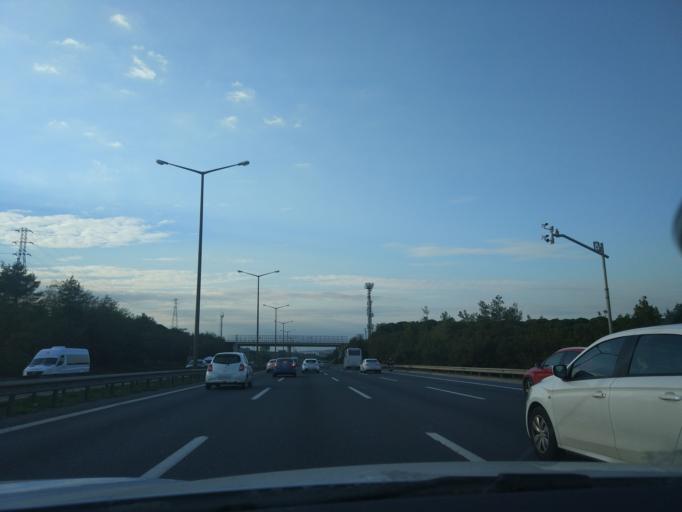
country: TR
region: Istanbul
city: Umraniye
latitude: 41.0644
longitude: 29.1126
